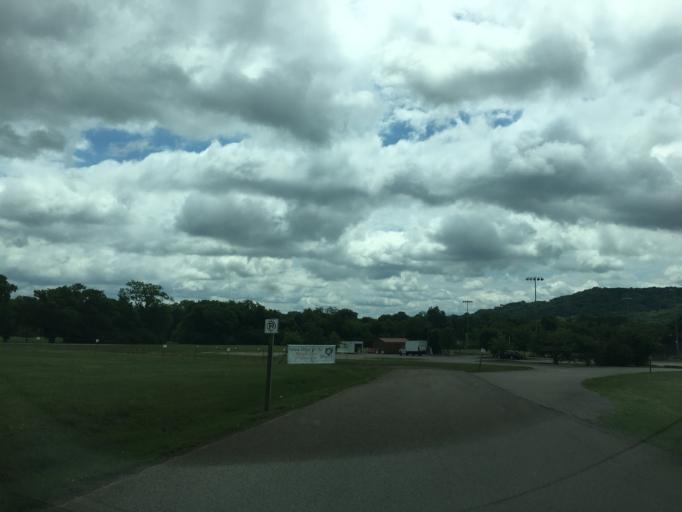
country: US
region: Tennessee
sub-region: Davidson County
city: Forest Hills
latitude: 36.0517
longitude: -86.8987
